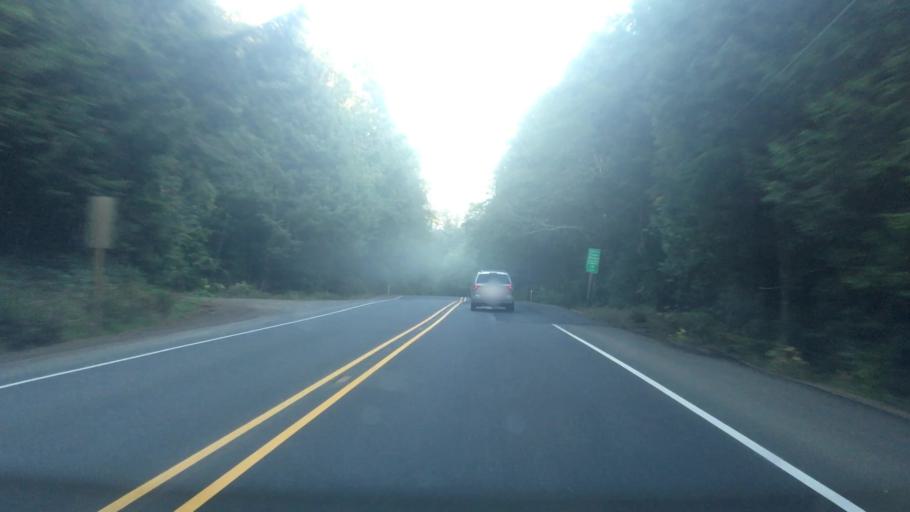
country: US
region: Oregon
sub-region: Clatsop County
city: Cannon Beach
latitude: 45.7811
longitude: -123.9557
